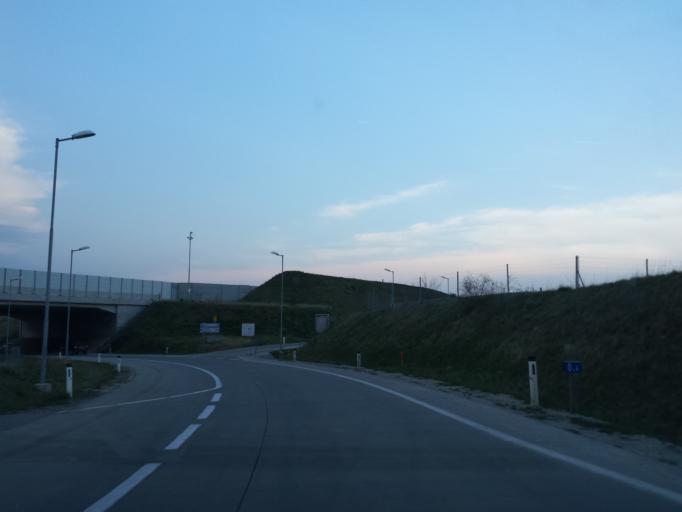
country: AT
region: Lower Austria
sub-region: Politischer Bezirk Mistelbach
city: Gaweinstal
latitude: 48.5172
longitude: 16.6213
